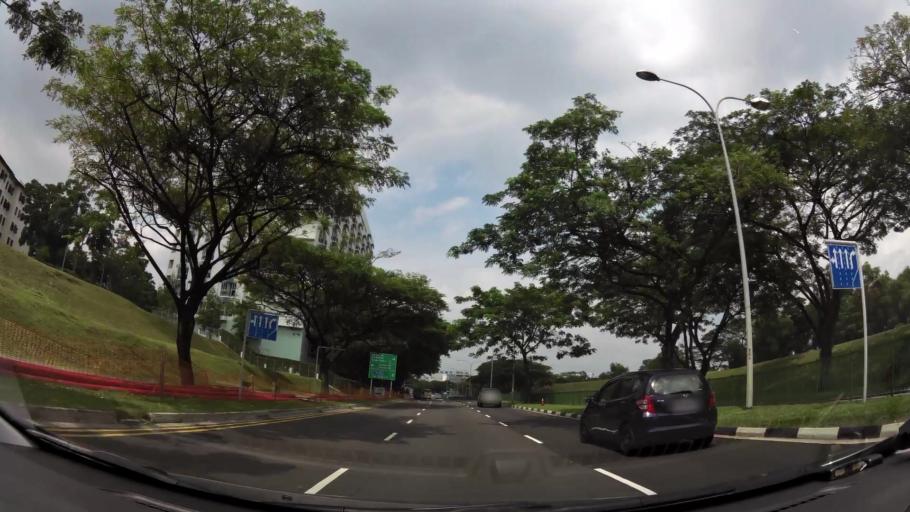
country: SG
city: Singapore
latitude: 1.3673
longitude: 103.9309
